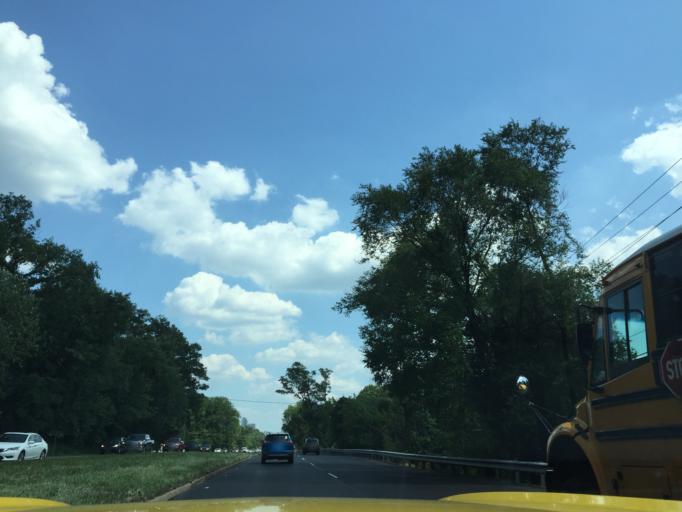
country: US
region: Virginia
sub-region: Fairfax County
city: Wolf Trap
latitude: 38.9492
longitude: -77.2616
